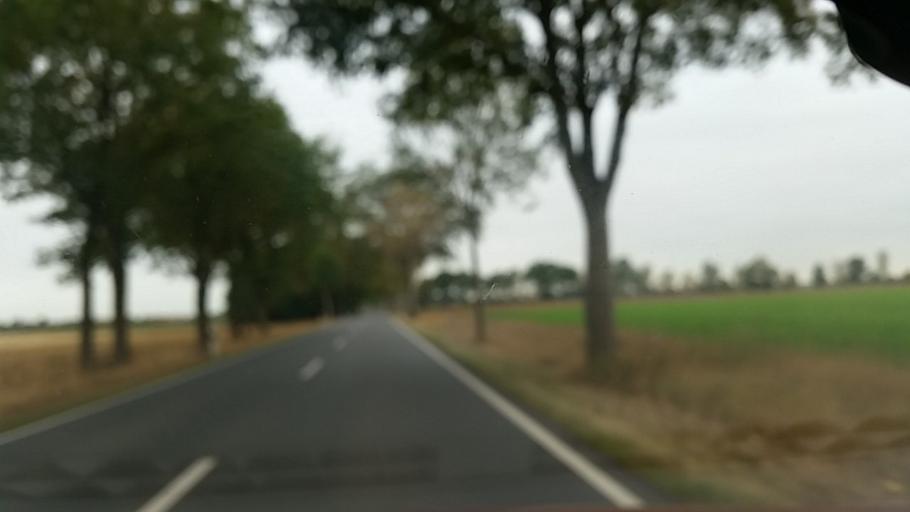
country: DE
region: Lower Saxony
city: Ummern
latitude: 52.5923
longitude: 10.4608
